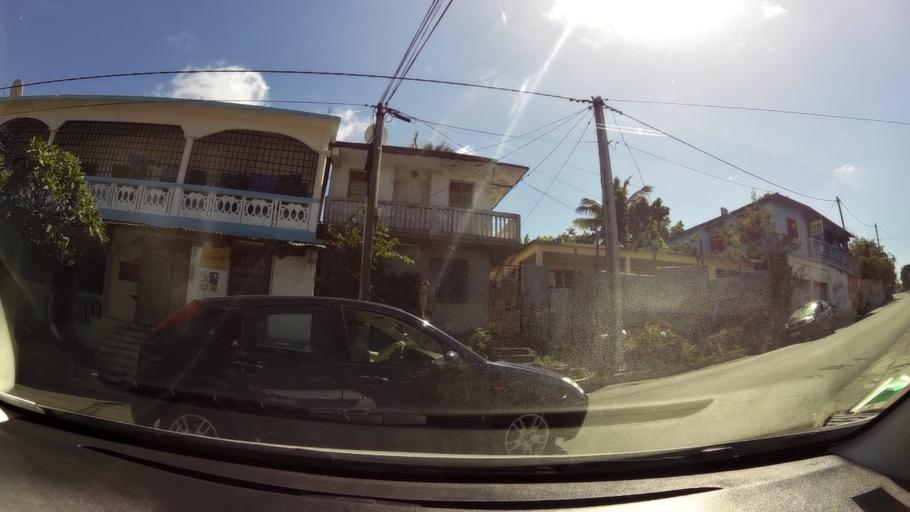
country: YT
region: Pamandzi
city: Pamandzi
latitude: -12.7929
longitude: 45.2800
